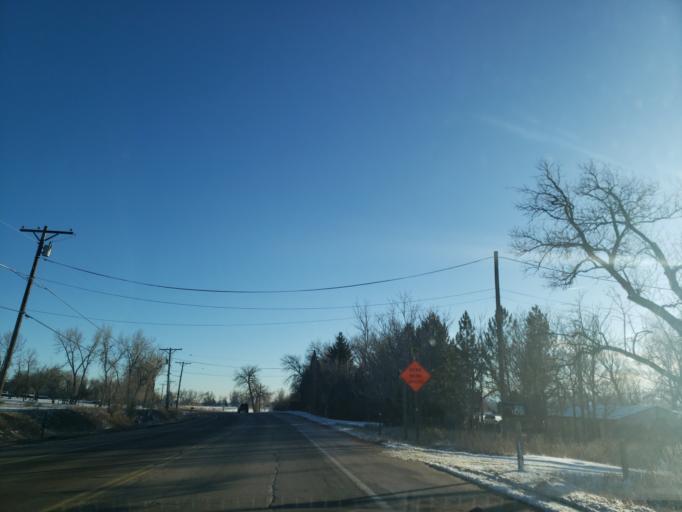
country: US
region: Colorado
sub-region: Larimer County
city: Fort Collins
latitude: 40.6218
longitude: -105.0722
